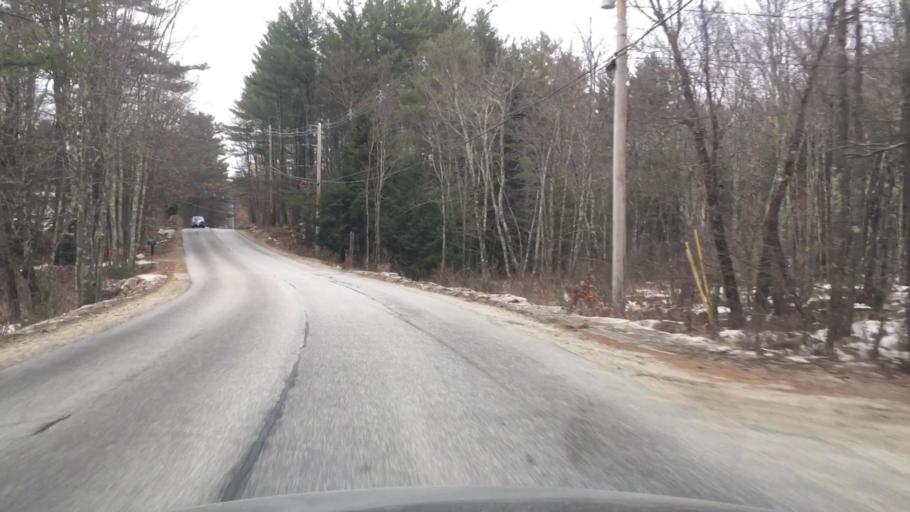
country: US
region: New Hampshire
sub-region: Hillsborough County
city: Goffstown
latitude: 42.9643
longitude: -71.6205
